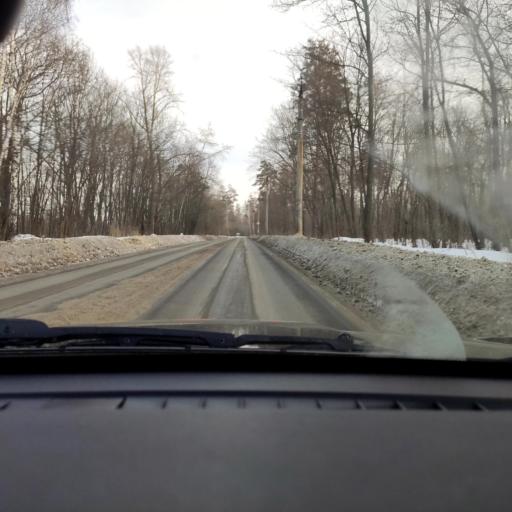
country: RU
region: Samara
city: Pribrezhnyy
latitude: 53.5157
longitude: 49.8476
